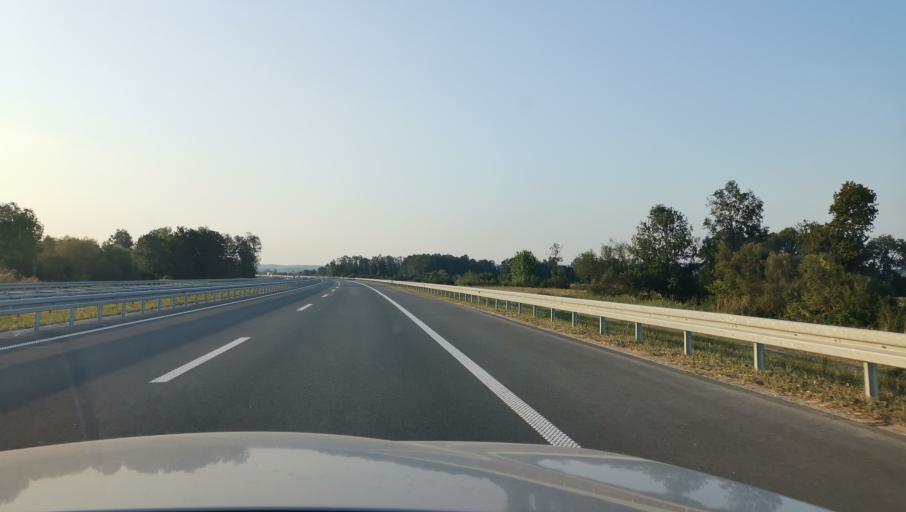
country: RS
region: Central Serbia
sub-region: Kolubarski Okrug
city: Ljig
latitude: 44.2657
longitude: 20.2704
